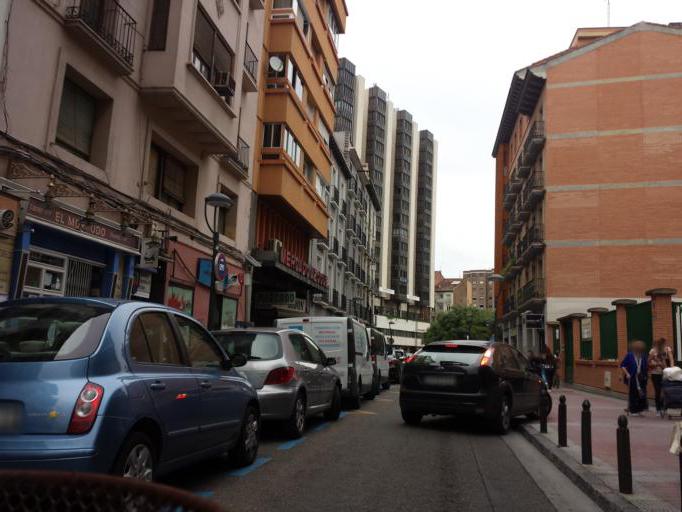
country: ES
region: Aragon
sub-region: Provincia de Zaragoza
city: Zaragoza
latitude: 41.6514
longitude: -0.8844
